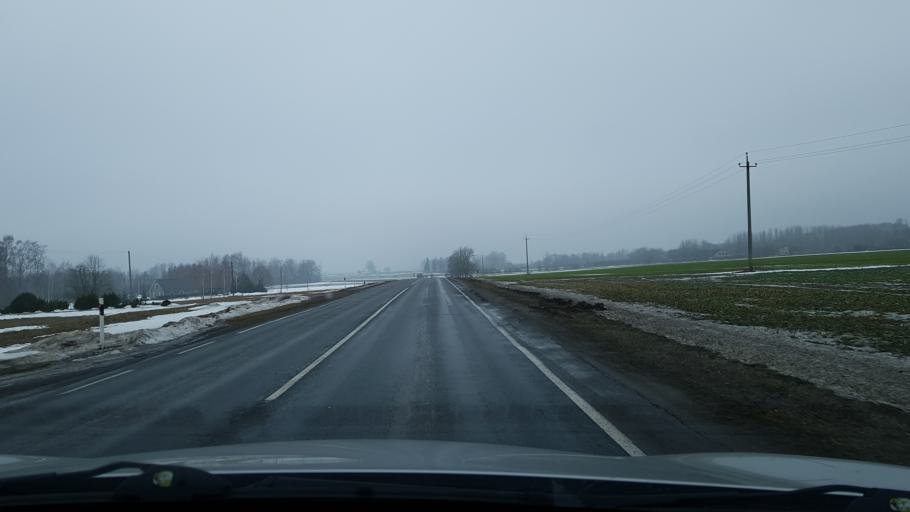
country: EE
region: Viljandimaa
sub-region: Viiratsi vald
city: Viiratsi
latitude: 58.2473
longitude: 25.8478
